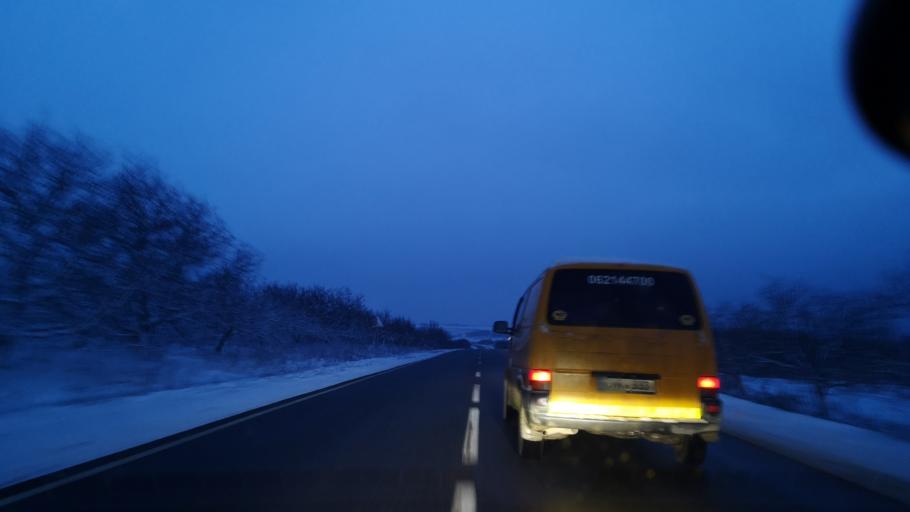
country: MD
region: Rezina
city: Saharna
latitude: 47.6158
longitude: 28.8320
